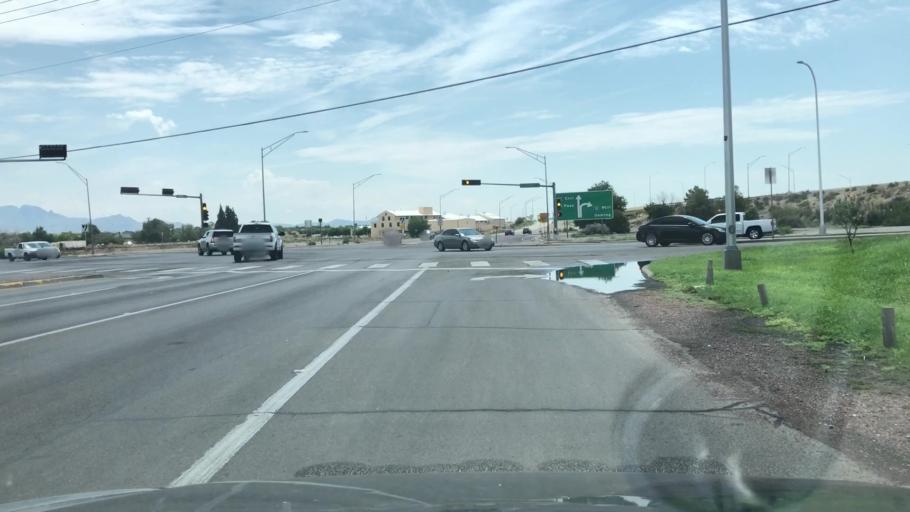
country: US
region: New Mexico
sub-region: Dona Ana County
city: University Park
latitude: 32.2821
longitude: -106.7685
